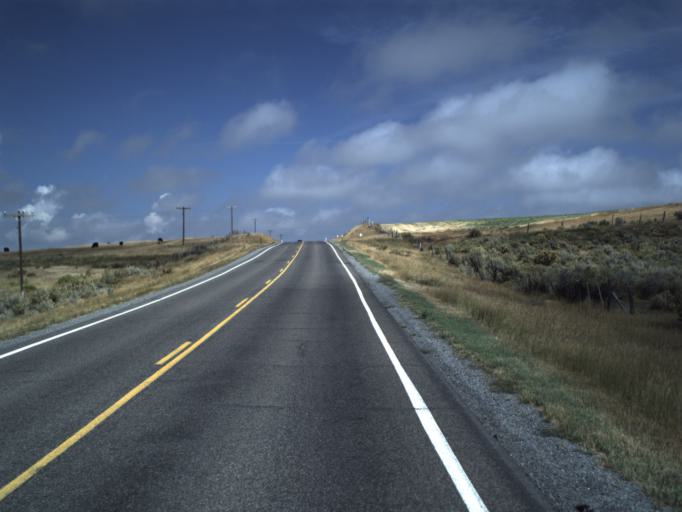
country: US
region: Utah
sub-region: Rich County
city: Randolph
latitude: 41.7259
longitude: -111.1591
